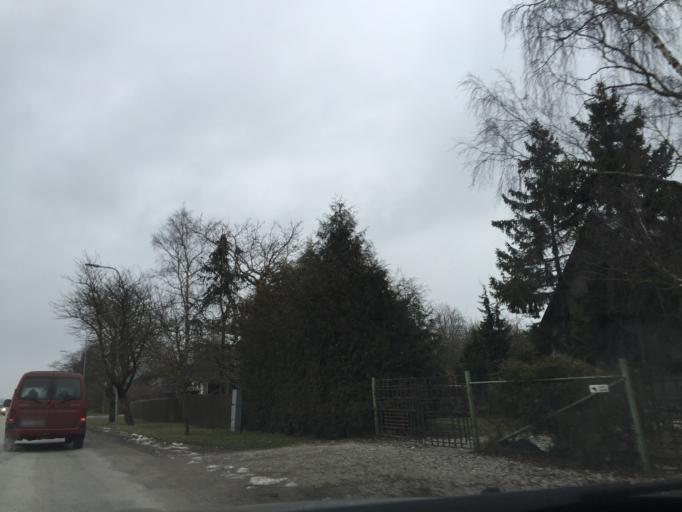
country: EE
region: Saare
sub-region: Kuressaare linn
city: Kuressaare
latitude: 58.2556
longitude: 22.4778
